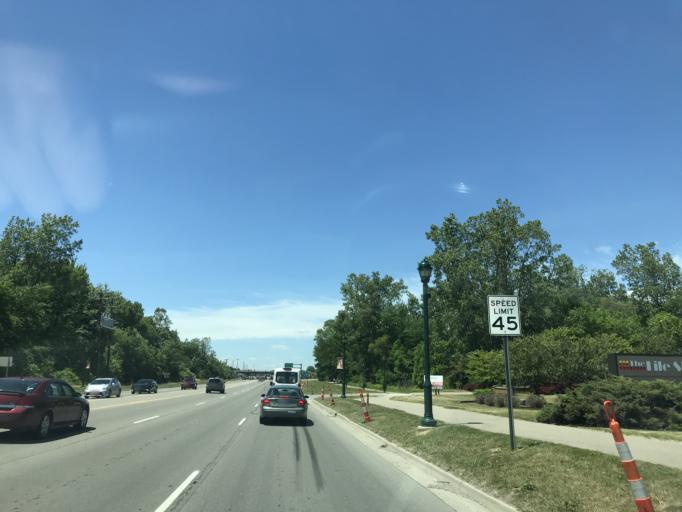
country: US
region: Michigan
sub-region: Wayne County
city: Westland
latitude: 42.3234
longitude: -83.4355
